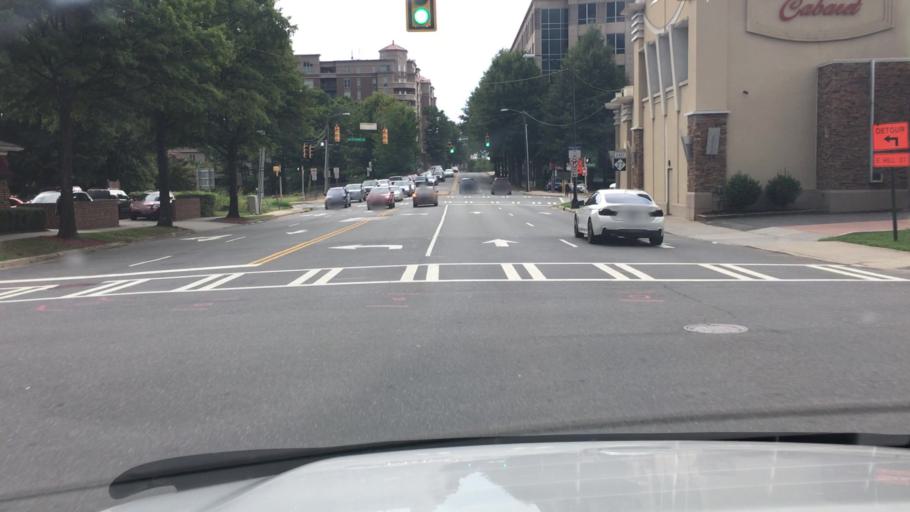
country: US
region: North Carolina
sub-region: Mecklenburg County
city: Charlotte
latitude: 35.2209
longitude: -80.8512
